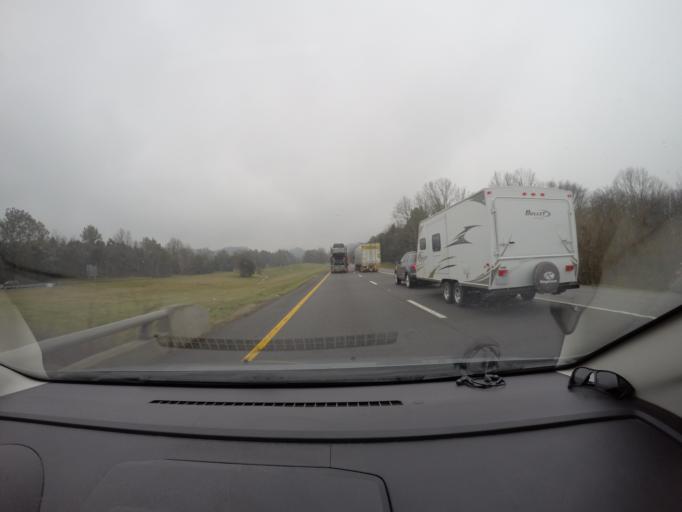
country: US
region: Tennessee
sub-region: Rutherford County
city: Plainview
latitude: 35.6076
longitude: -86.2404
